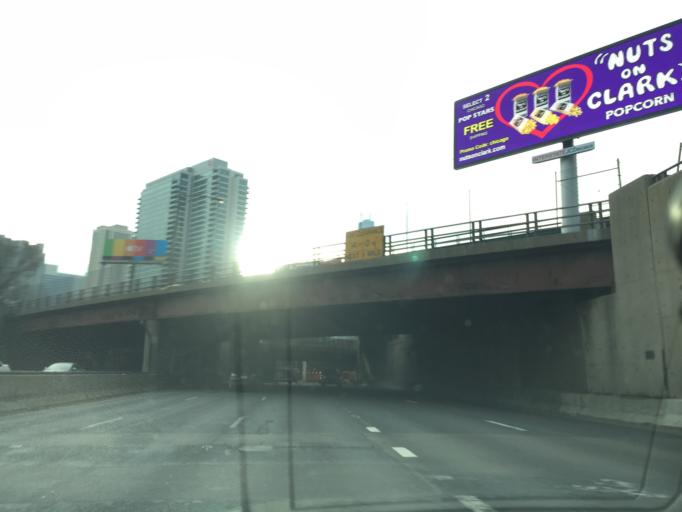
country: US
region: Illinois
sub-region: Cook County
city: Chicago
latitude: 41.8904
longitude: -87.6501
